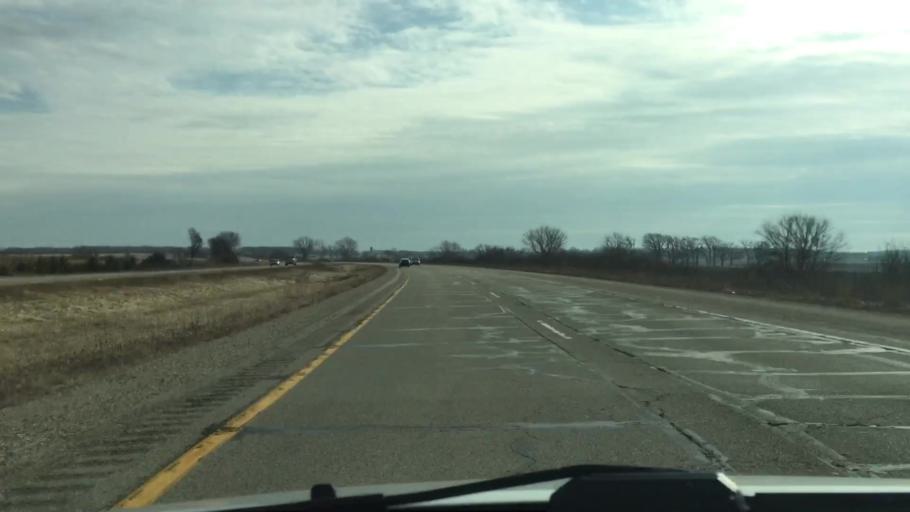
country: US
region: Wisconsin
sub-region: Walworth County
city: Como
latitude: 42.6456
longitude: -88.5016
